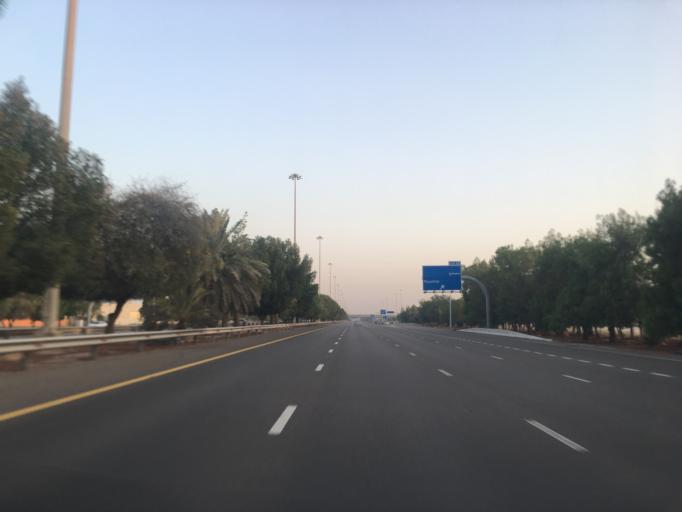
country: AE
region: Abu Dhabi
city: Abu Dhabi
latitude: 24.3692
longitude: 54.5578
